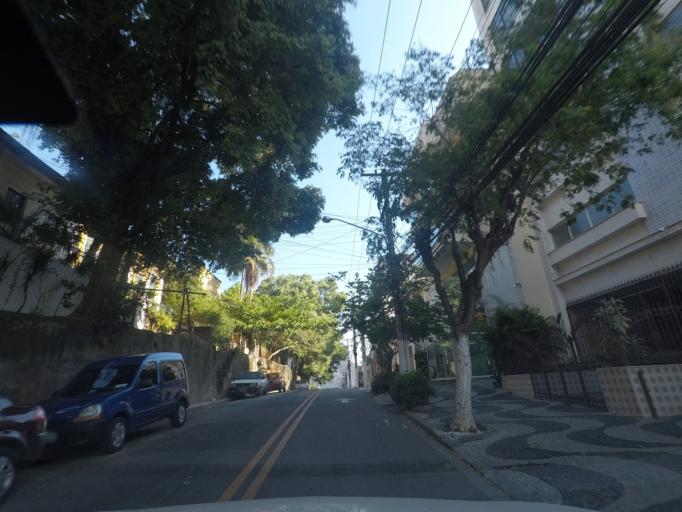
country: BR
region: Rio de Janeiro
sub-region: Niteroi
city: Niteroi
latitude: -22.9064
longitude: -43.1300
